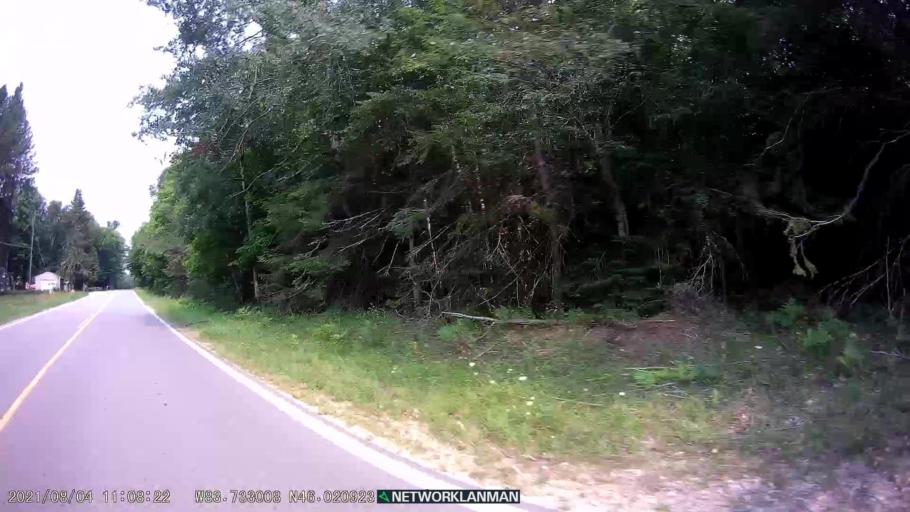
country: CA
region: Ontario
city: Thessalon
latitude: 46.0215
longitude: -83.7334
